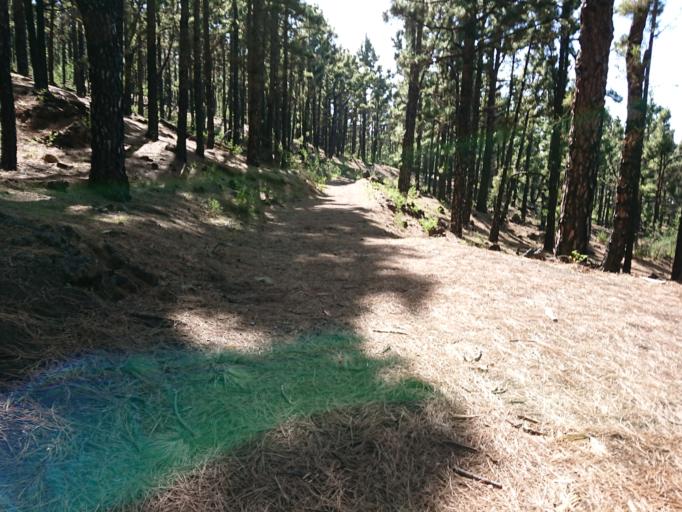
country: ES
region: Canary Islands
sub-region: Provincia de Santa Cruz de Tenerife
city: El Paso
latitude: 28.5944
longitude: -17.8619
